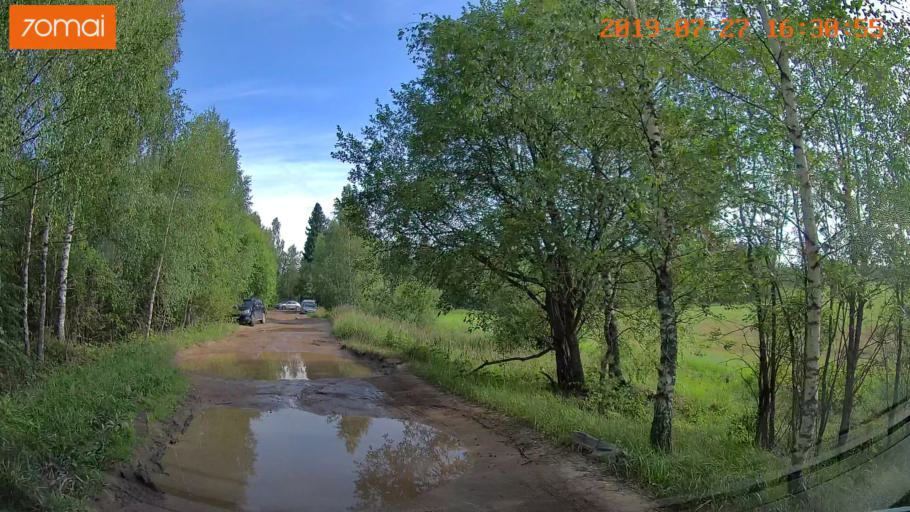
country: RU
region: Ivanovo
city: Novo-Talitsy
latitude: 57.0915
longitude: 40.8525
